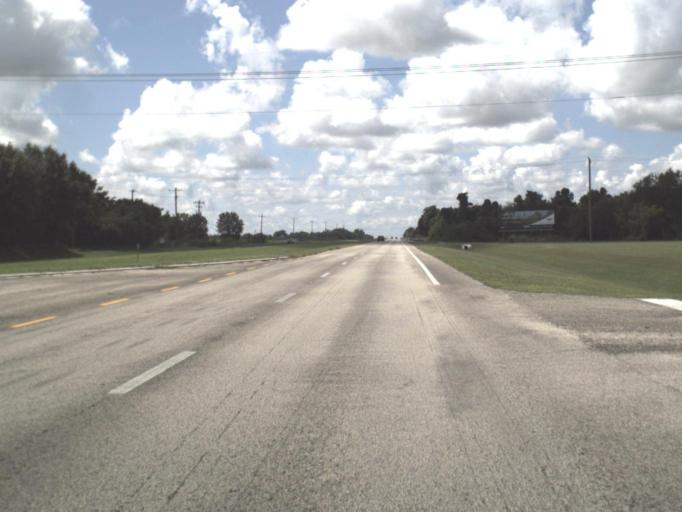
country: US
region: Florida
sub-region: DeSoto County
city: Arcadia
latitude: 27.3094
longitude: -81.8191
